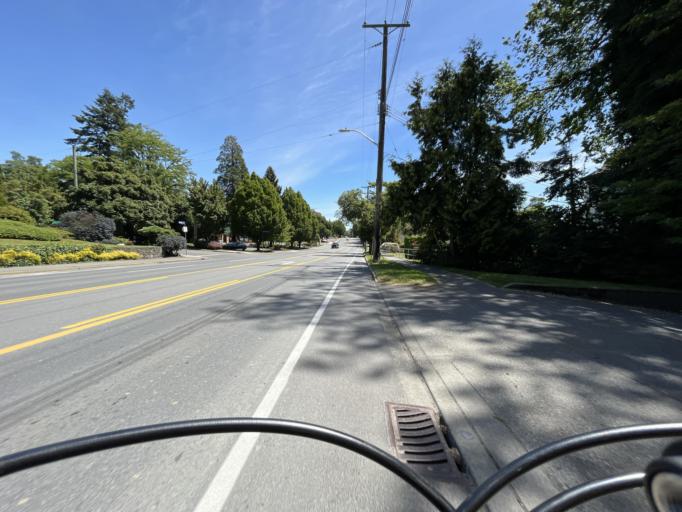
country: CA
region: British Columbia
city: Victoria
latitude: 48.4433
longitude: -123.3855
